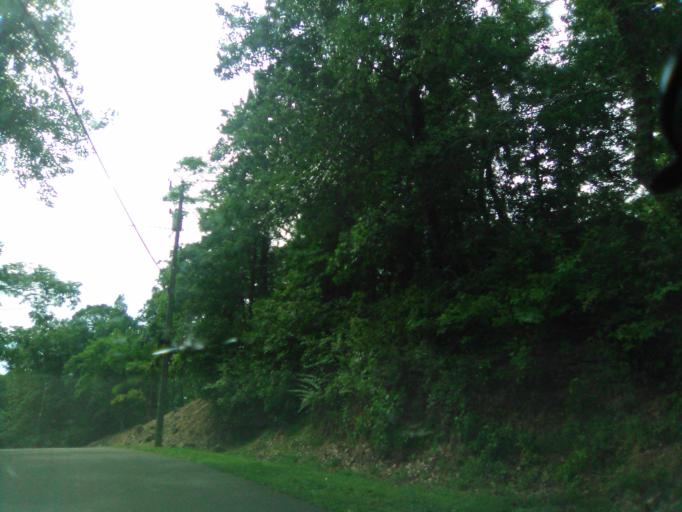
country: US
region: Tennessee
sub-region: Davidson County
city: Belle Meade
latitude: 36.0964
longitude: -86.8981
